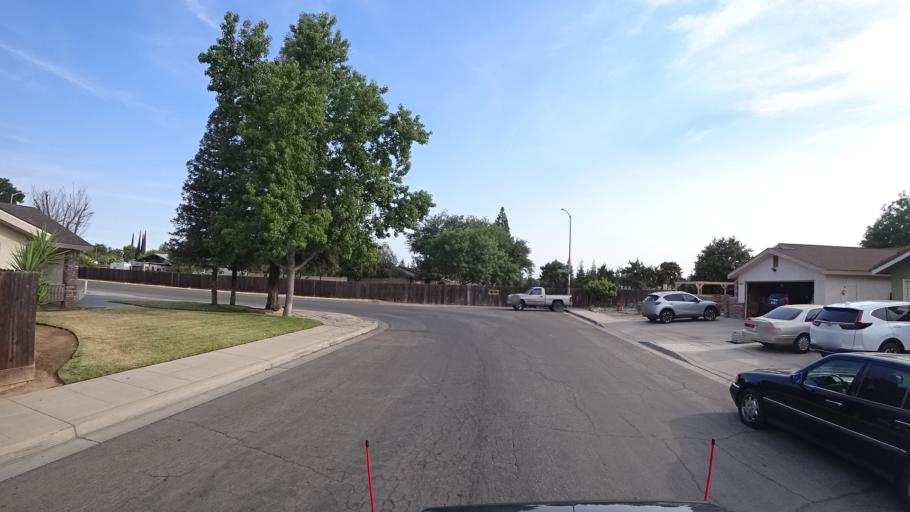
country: US
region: California
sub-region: Fresno County
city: West Park
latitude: 36.7757
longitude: -119.8630
